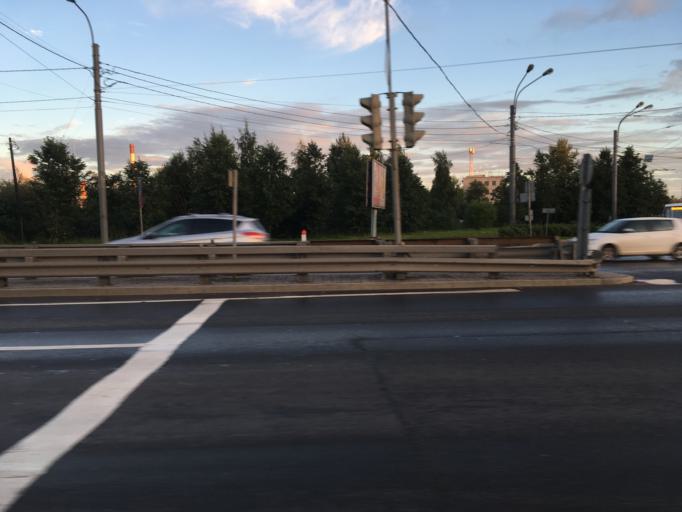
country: RU
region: Leningrad
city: Rybatskoye
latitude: 59.8851
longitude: 30.4902
